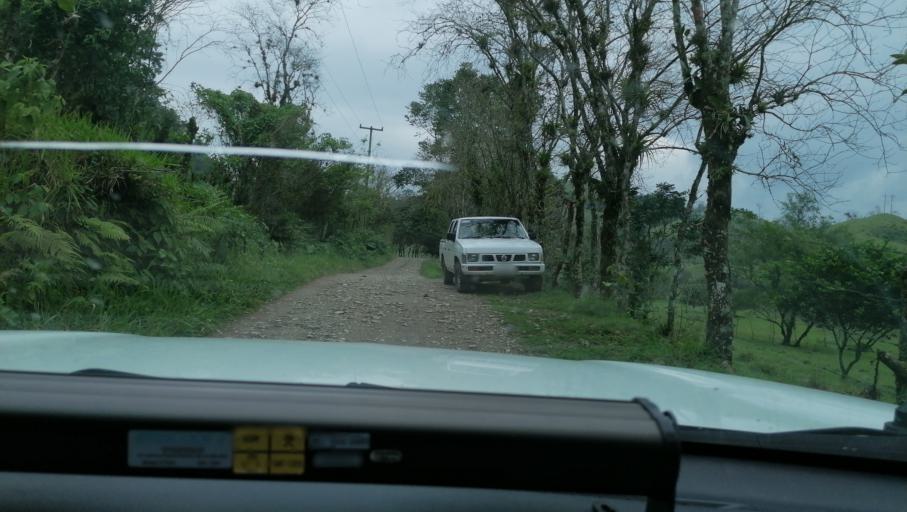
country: MX
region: Chiapas
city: Ixtacomitan
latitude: 17.3517
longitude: -93.1533
